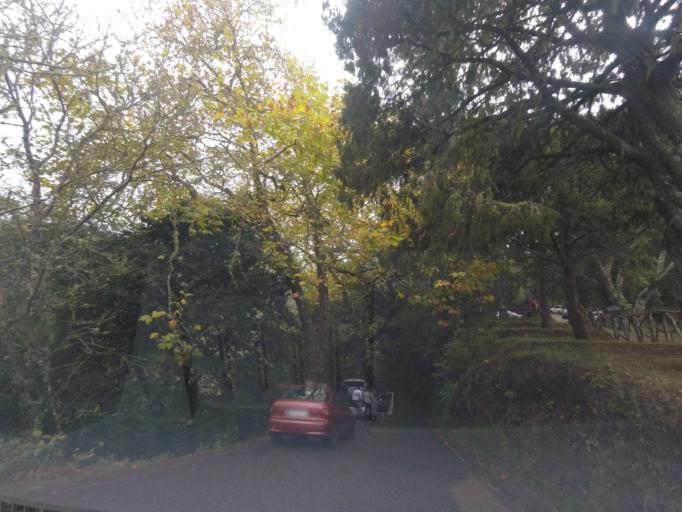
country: PT
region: Madeira
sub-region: Santana
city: Santana
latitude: 32.7822
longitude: -16.9067
